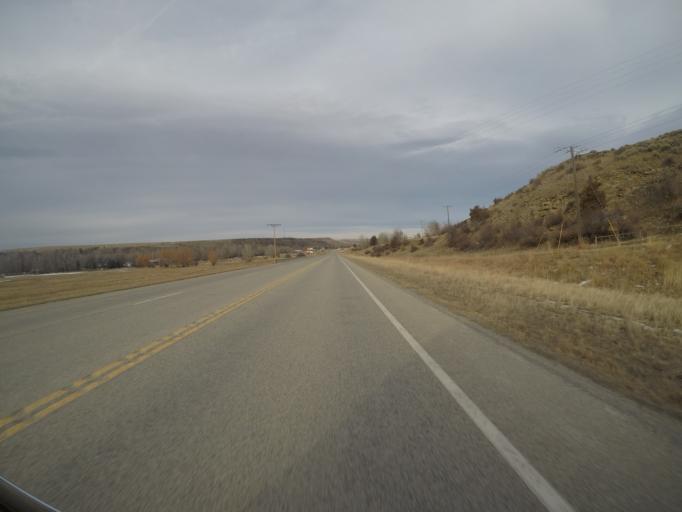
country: US
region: Montana
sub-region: Stillwater County
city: Absarokee
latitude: 45.5019
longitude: -109.4488
